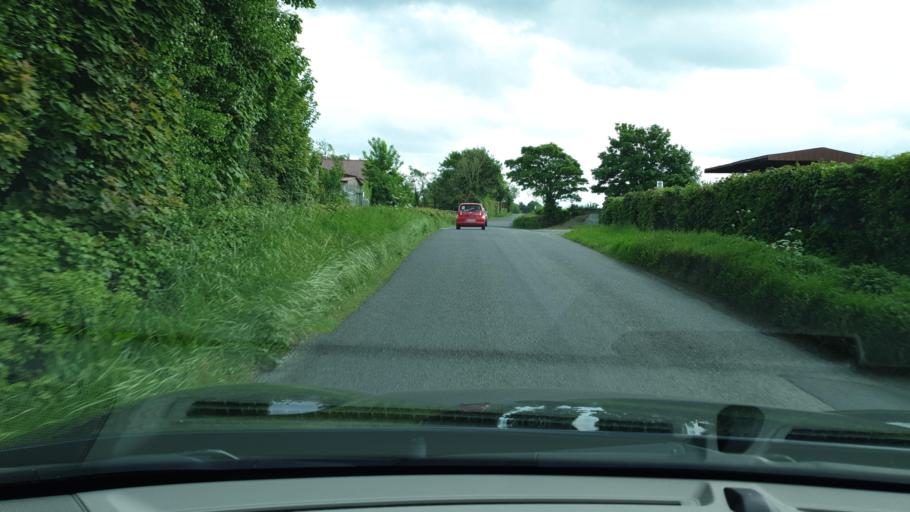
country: IE
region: Leinster
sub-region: An Mhi
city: Ashbourne
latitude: 53.4977
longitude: -6.3726
